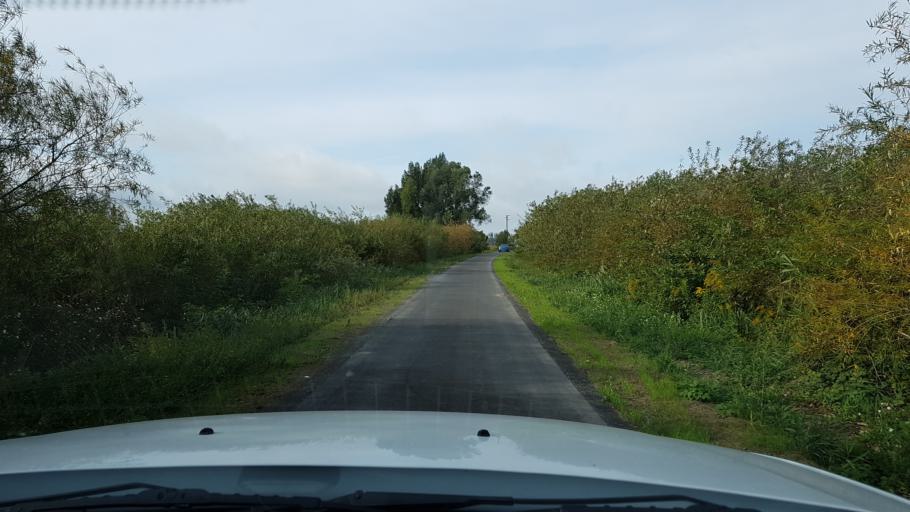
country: PL
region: West Pomeranian Voivodeship
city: Trzcinsko Zdroj
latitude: 52.9601
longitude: 14.6140
